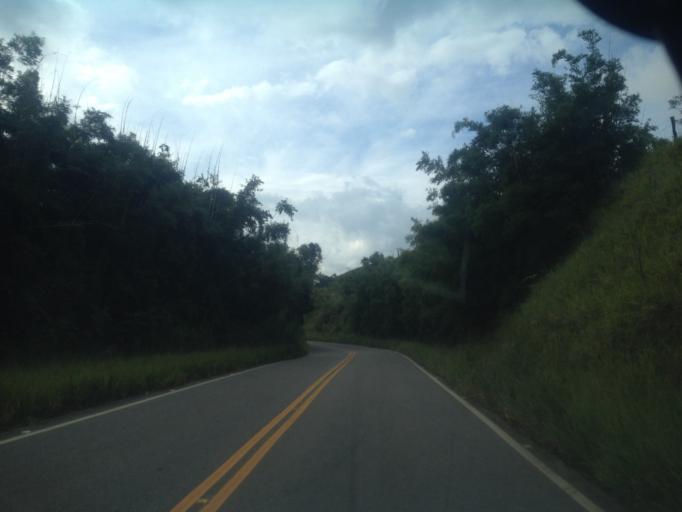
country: BR
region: Rio de Janeiro
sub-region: Quatis
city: Quatis
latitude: -22.3646
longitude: -44.2563
